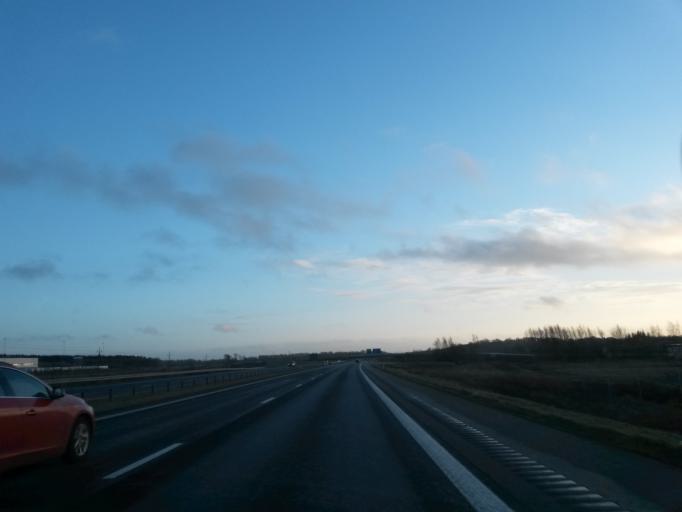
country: SE
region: Halland
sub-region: Halmstads Kommun
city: Halmstad
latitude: 56.7207
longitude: 12.8848
